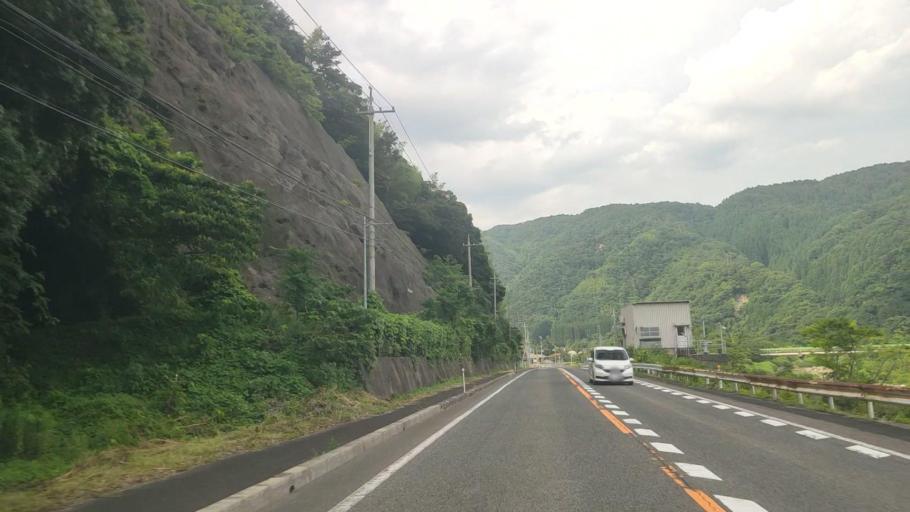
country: JP
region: Tottori
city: Kurayoshi
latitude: 35.3638
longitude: 133.8472
